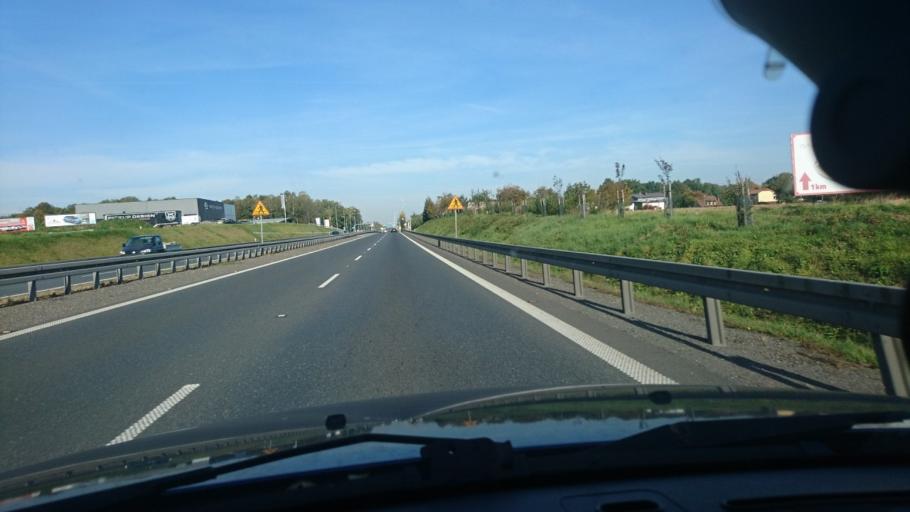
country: PL
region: Silesian Voivodeship
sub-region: Powiat bielski
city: Mazancowice
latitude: 49.8660
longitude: 19.0116
